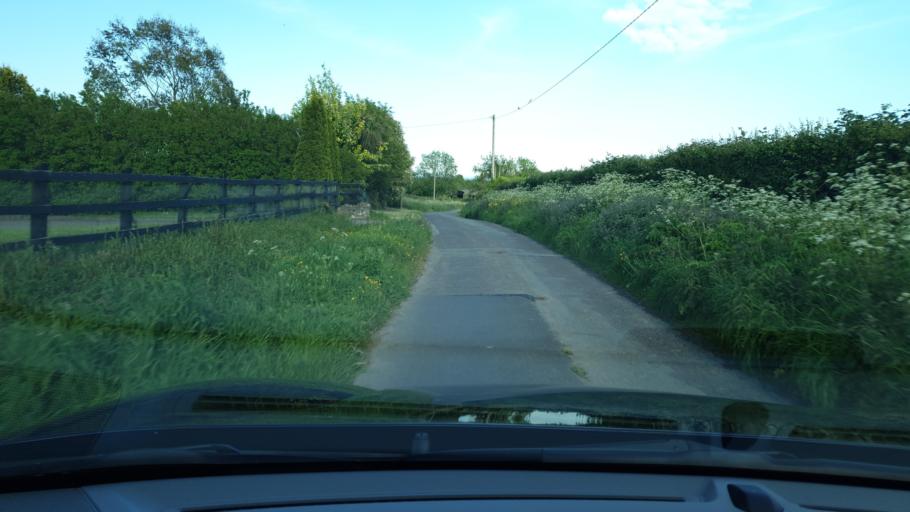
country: IE
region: Leinster
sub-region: An Mhi
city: Ashbourne
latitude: 53.5584
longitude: -6.3725
